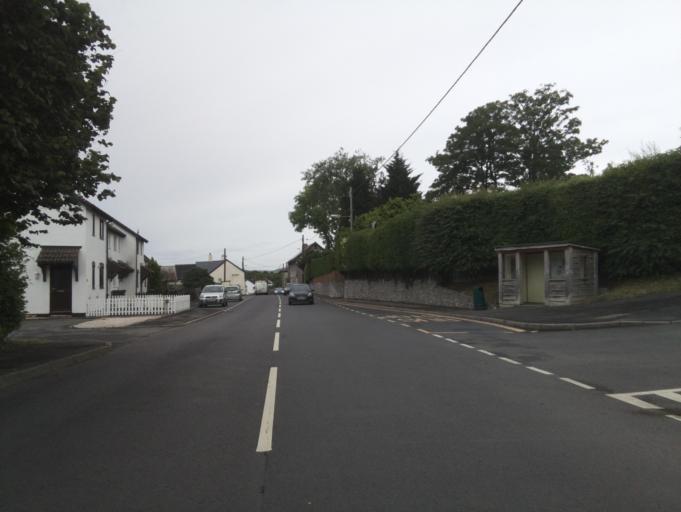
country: GB
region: England
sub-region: Devon
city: Chudleigh
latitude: 50.5860
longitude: -3.6295
